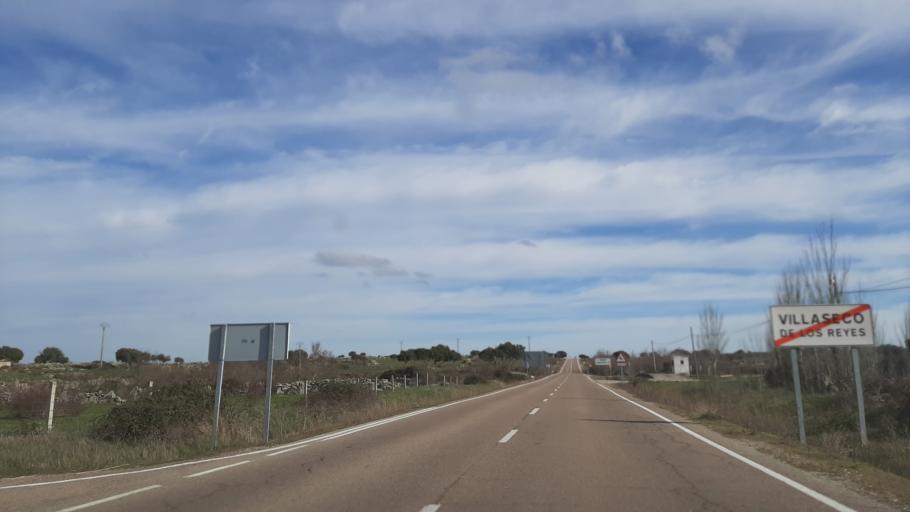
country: ES
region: Castille and Leon
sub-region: Provincia de Salamanca
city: Villaseco de los Reyes
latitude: 41.1626
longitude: -6.1821
